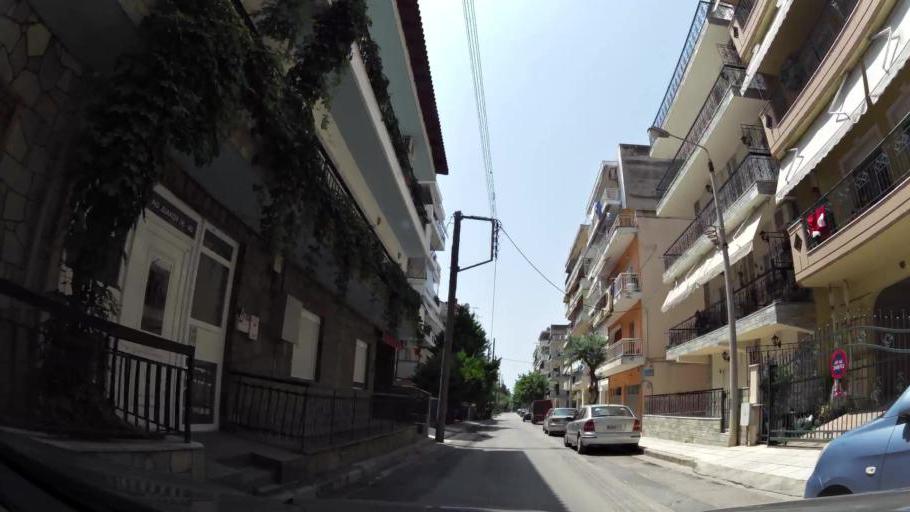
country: GR
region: Central Macedonia
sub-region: Nomos Thessalonikis
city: Menemeni
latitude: 40.6721
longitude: 22.8912
